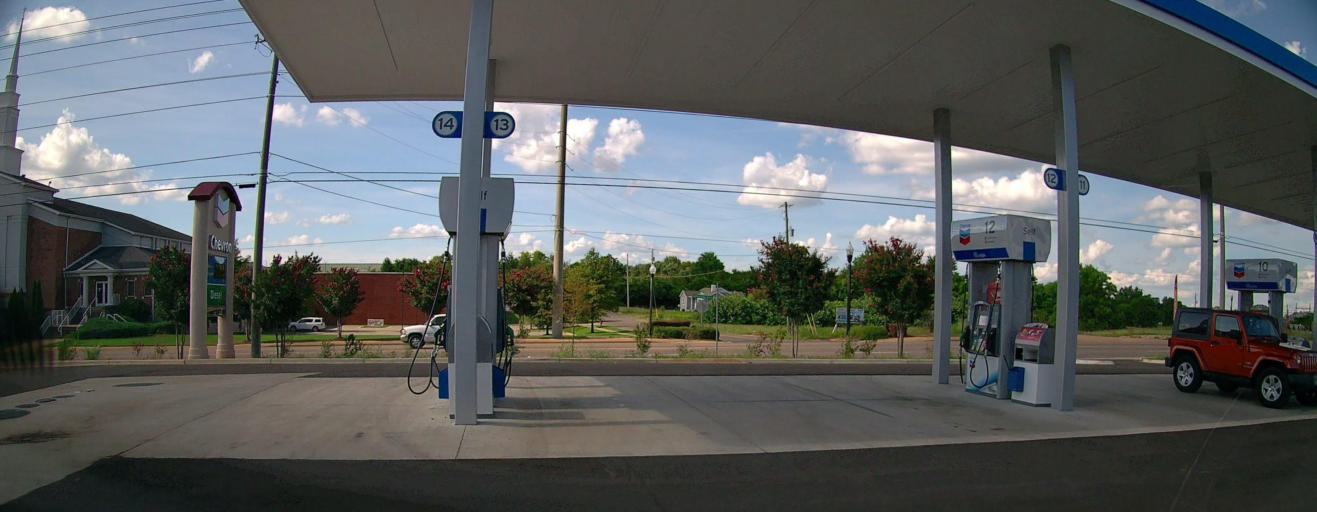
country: US
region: Alabama
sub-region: Tuscaloosa County
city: Holt
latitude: 33.2059
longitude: -87.5085
